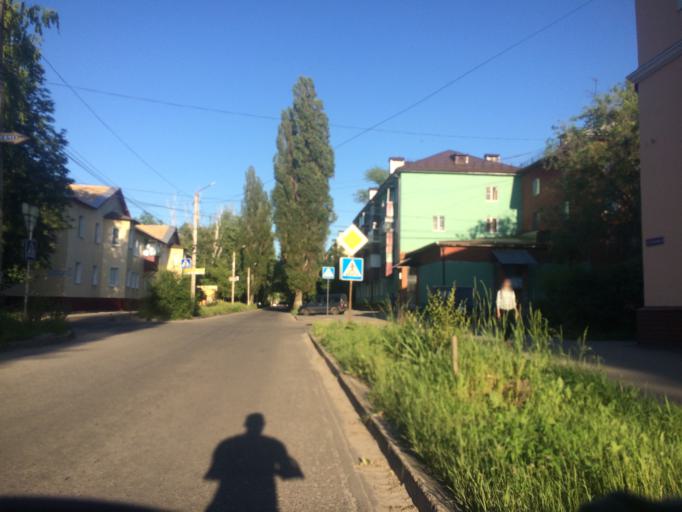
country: RU
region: Kursk
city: Kursk
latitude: 51.6727
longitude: 36.1482
